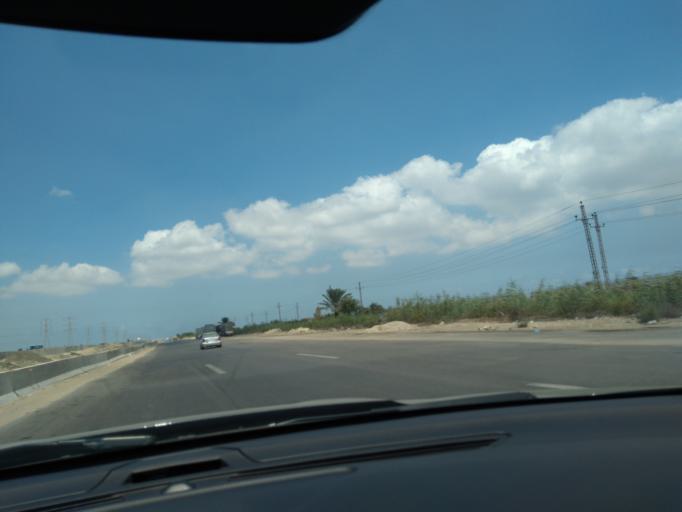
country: EG
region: Muhafazat Bur Sa`id
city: Port Said
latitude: 31.1556
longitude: 32.3020
